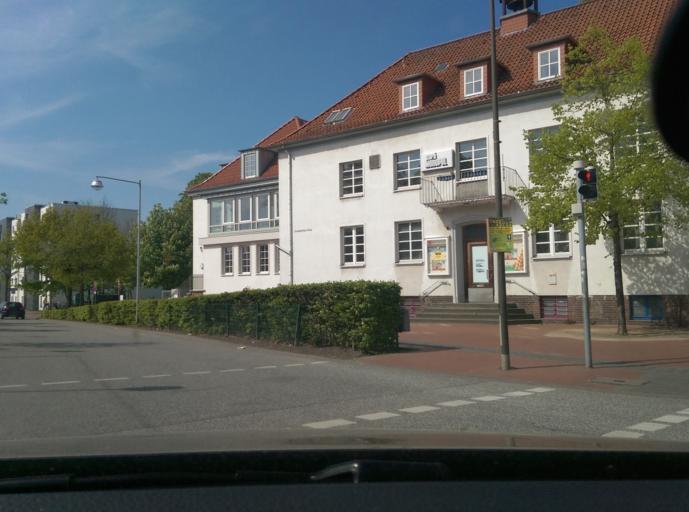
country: DE
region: Lower Saxony
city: Langenhagen
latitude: 52.4385
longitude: 9.7340
